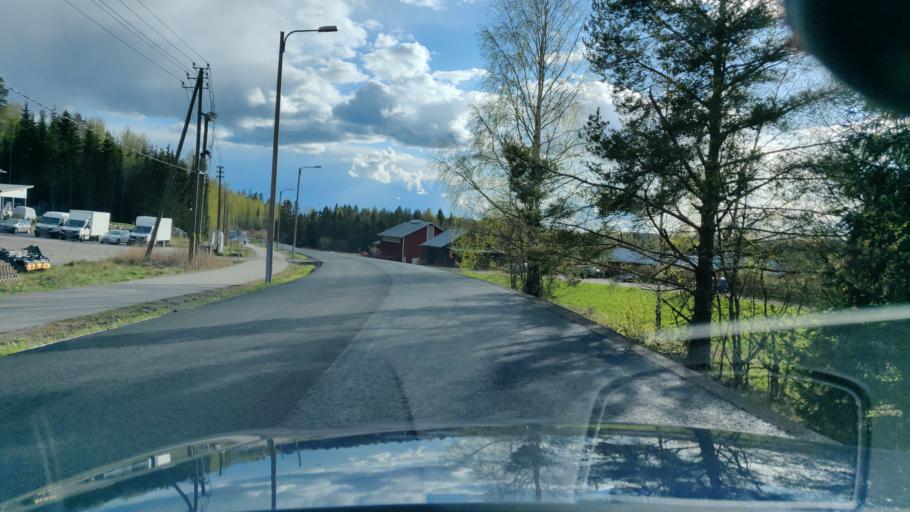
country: FI
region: Uusimaa
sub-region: Helsinki
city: Nurmijaervi
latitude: 60.3745
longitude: 24.7395
